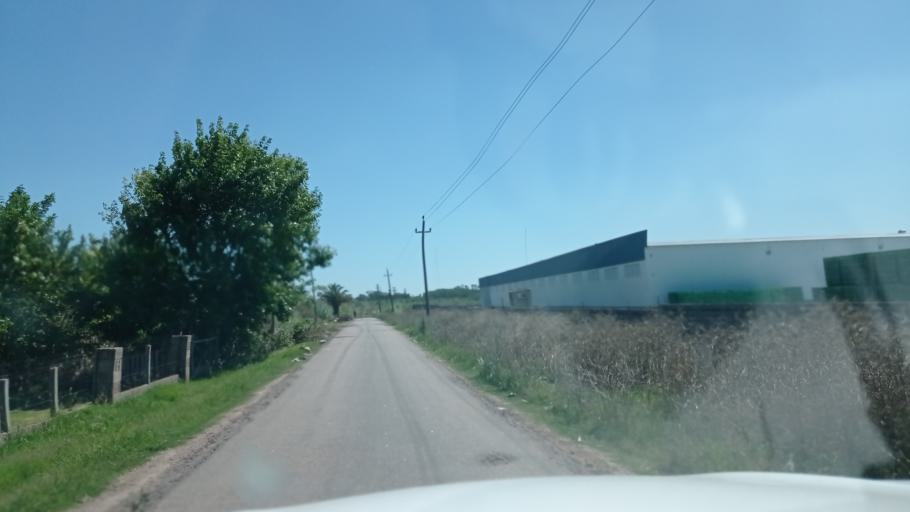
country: UY
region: Montevideo
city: Pajas Blancas
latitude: -34.8706
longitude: -56.2843
